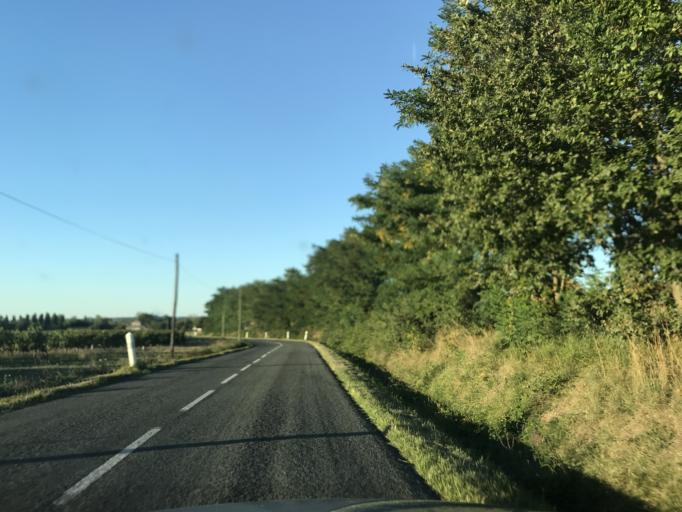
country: FR
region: Aquitaine
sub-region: Departement de la Gironde
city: Saint-Medard-de-Guizieres
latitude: 44.9996
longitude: -0.0546
